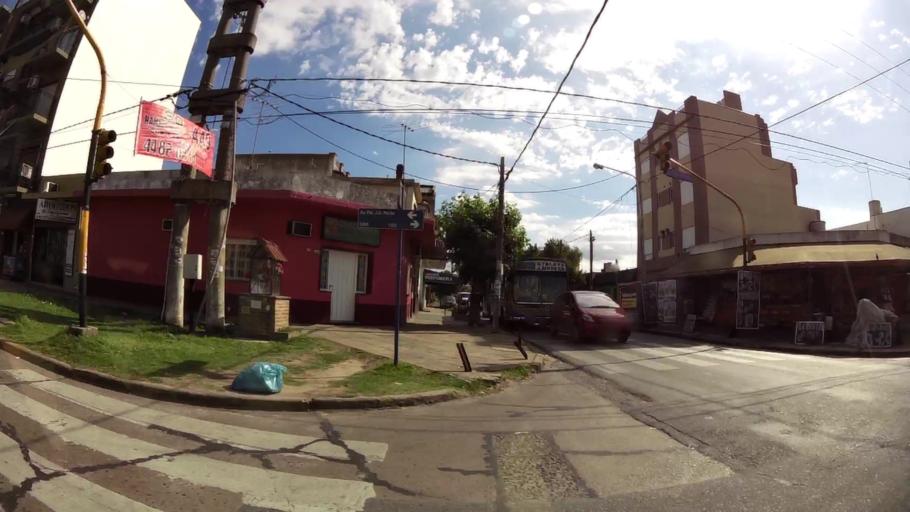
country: AR
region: Buenos Aires
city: San Justo
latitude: -34.6617
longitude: -58.5764
